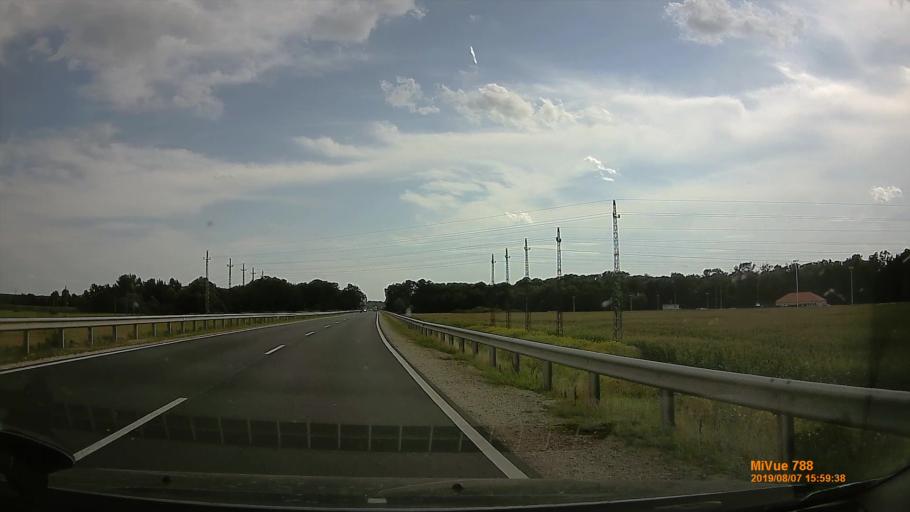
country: HU
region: Vas
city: Kormend
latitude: 47.0150
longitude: 16.6179
